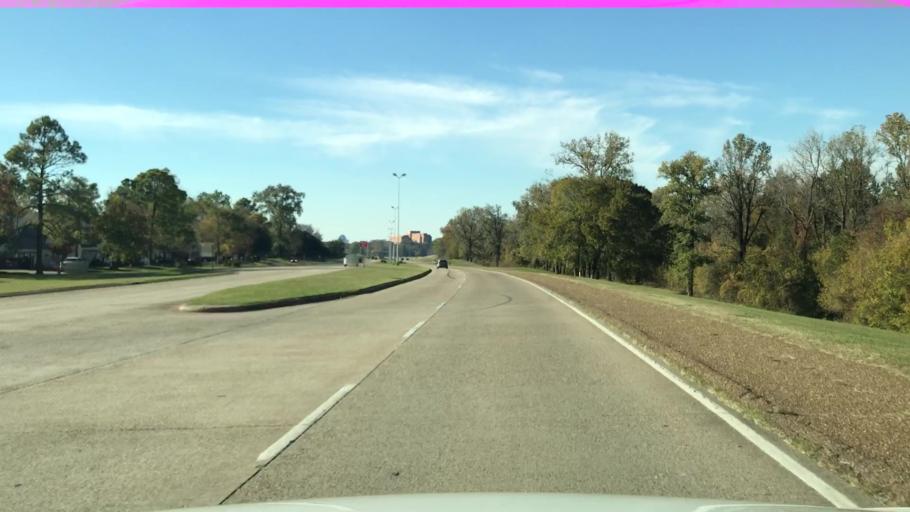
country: US
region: Louisiana
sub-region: Bossier Parish
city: Bossier City
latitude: 32.4920
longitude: -93.7022
